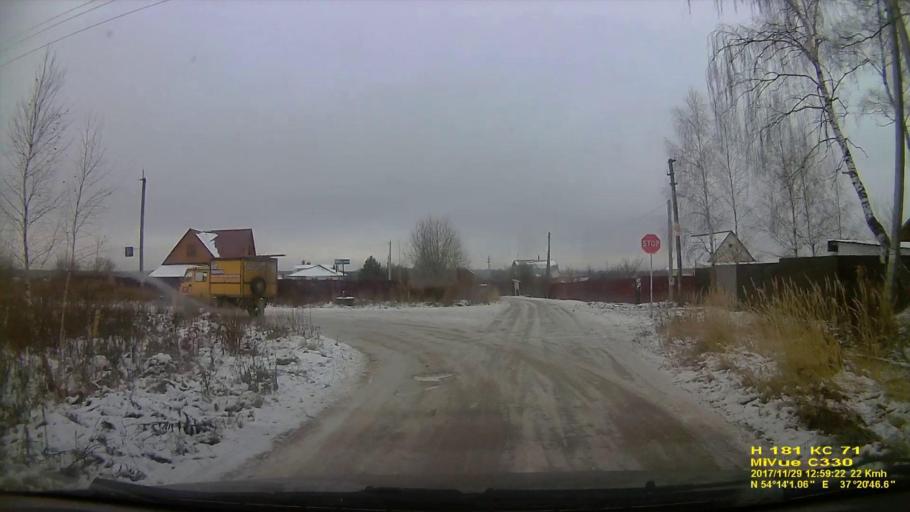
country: RU
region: Tula
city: Leninskiy
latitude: 54.2337
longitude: 37.3462
